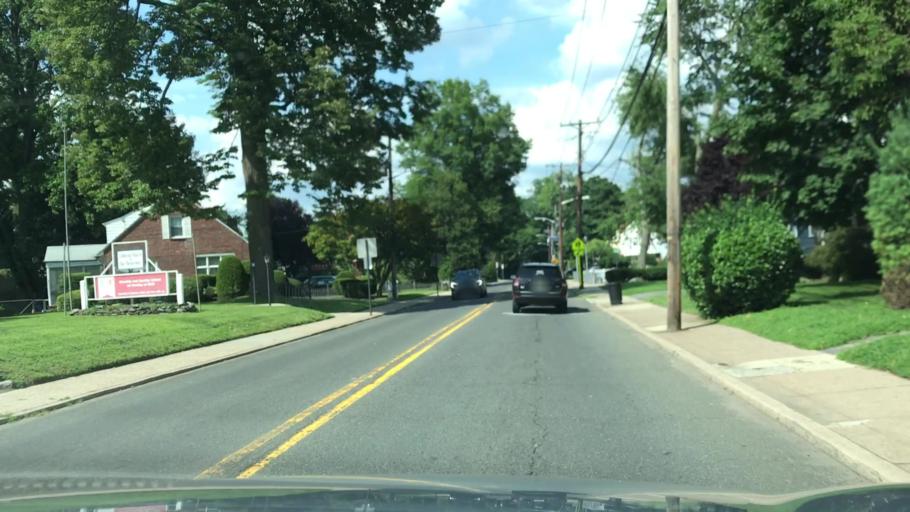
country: US
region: New Jersey
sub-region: Bergen County
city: Dumont
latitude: 40.9460
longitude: -73.9913
